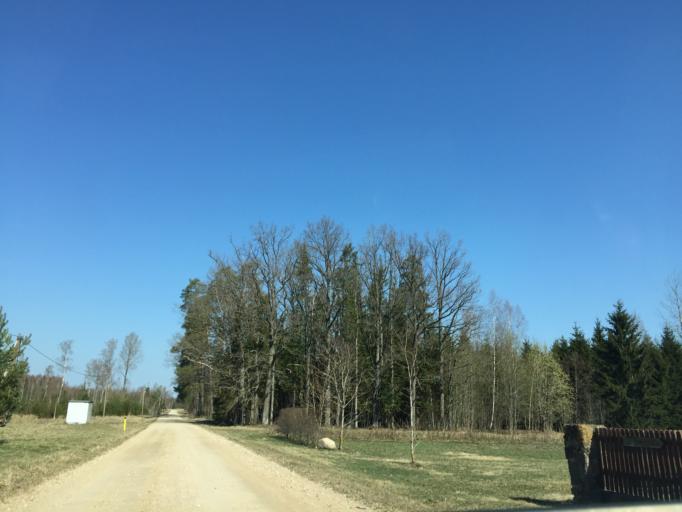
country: EE
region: Tartu
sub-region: Alatskivi vald
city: Kallaste
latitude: 58.5382
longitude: 26.9452
